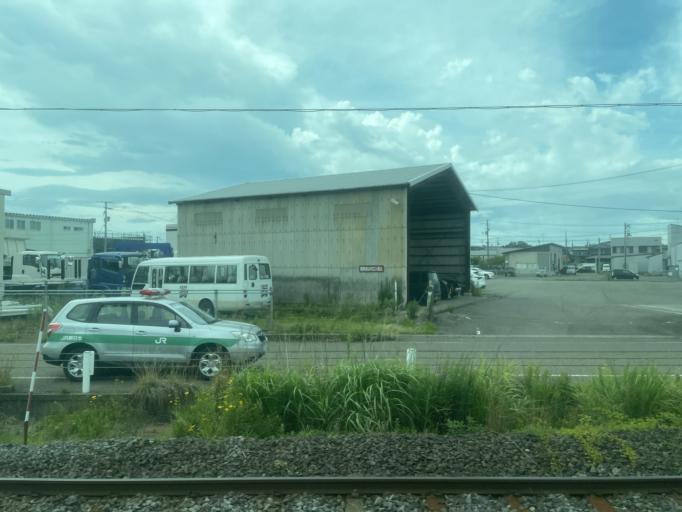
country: JP
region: Niigata
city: Joetsu
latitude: 37.1916
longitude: 138.2759
